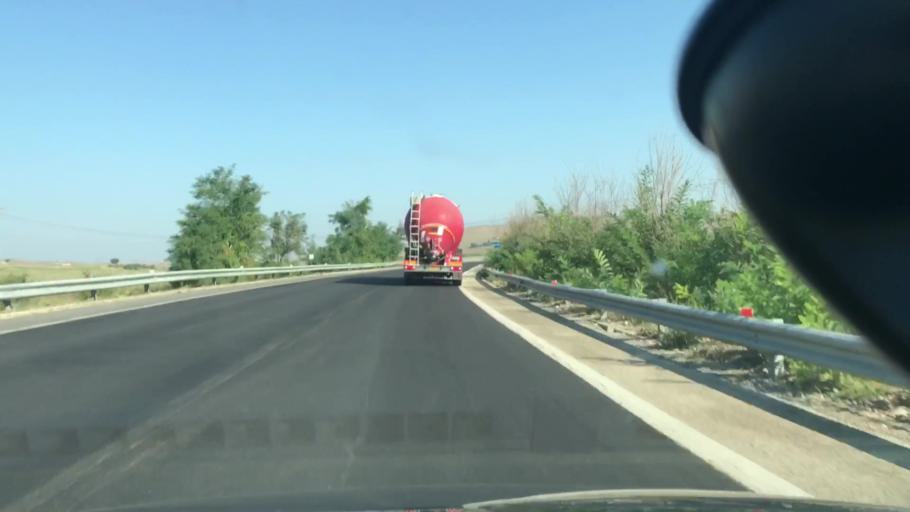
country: IT
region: Basilicate
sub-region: Provincia di Matera
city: Irsina
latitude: 40.7966
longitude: 16.2755
